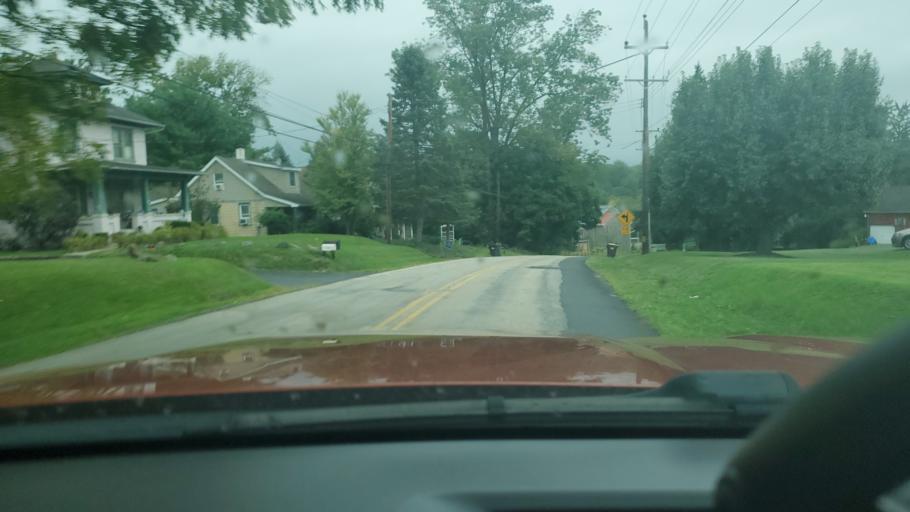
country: US
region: Pennsylvania
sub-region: Montgomery County
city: Woxall
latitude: 40.3224
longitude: -75.4829
